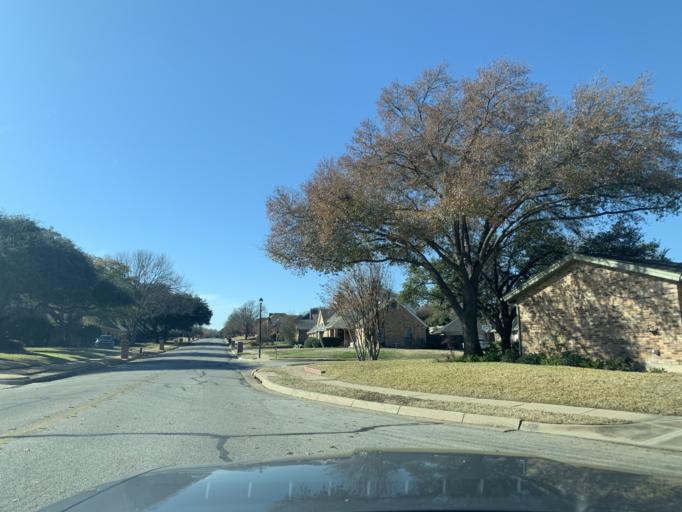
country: US
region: Texas
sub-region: Tarrant County
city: Bedford
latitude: 32.8462
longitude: -97.1541
